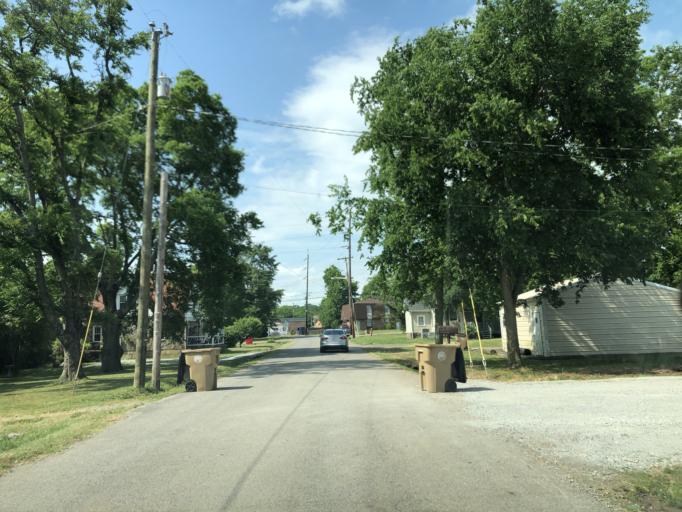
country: US
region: Tennessee
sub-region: Davidson County
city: Goodlettsville
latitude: 36.2609
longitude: -86.7054
